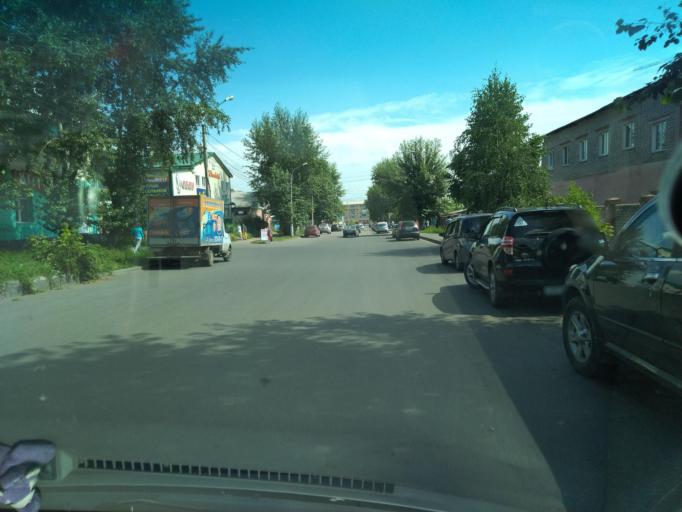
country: RU
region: Krasnoyarskiy
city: Krasnoyarsk
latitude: 56.0285
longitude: 92.8933
